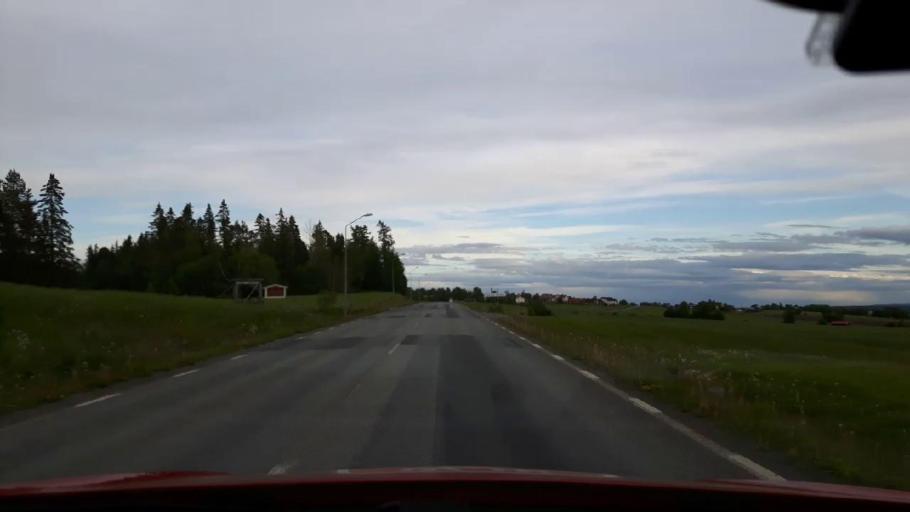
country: SE
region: Jaemtland
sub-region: OEstersunds Kommun
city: Ostersund
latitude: 63.1130
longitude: 14.4343
